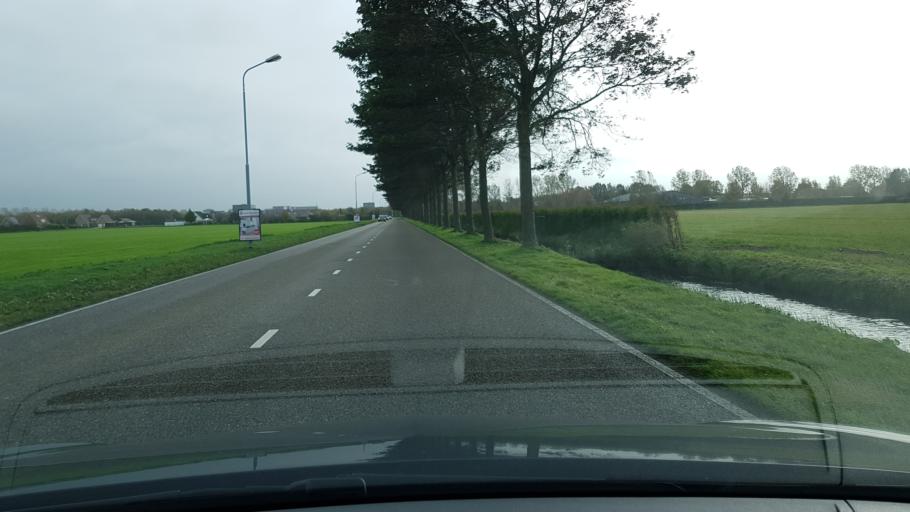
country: NL
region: North Holland
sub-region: Gemeente Heemstede
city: Heemstede
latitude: 52.3296
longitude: 4.6390
